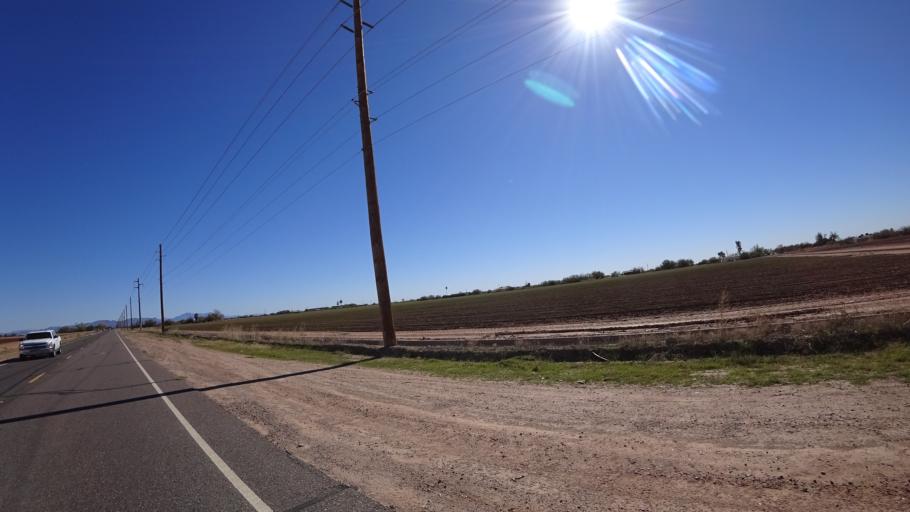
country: US
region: Arizona
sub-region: Maricopa County
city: Scottsdale
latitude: 33.4949
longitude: -111.8798
